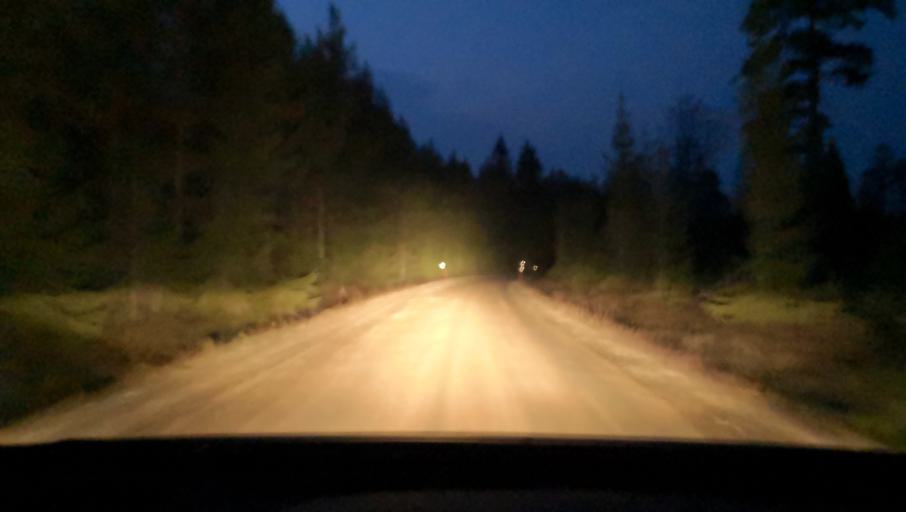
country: SE
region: OErebro
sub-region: Lindesbergs Kommun
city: Frovi
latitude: 59.6533
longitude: 15.4877
